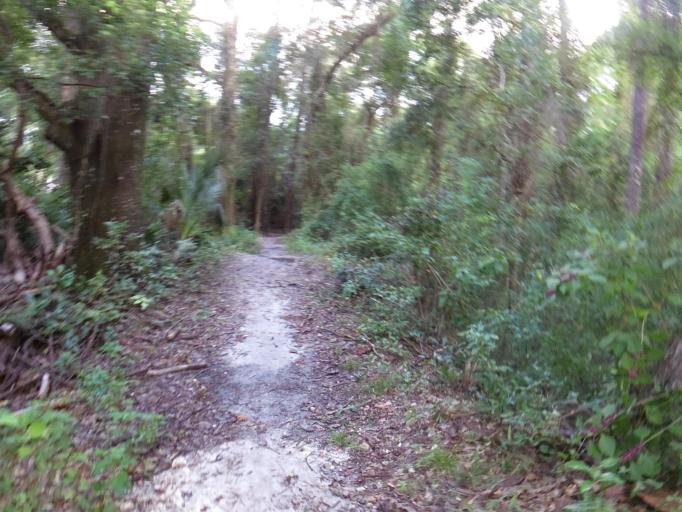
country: US
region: Florida
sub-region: Duval County
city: Jacksonville
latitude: 30.3281
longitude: -81.7803
